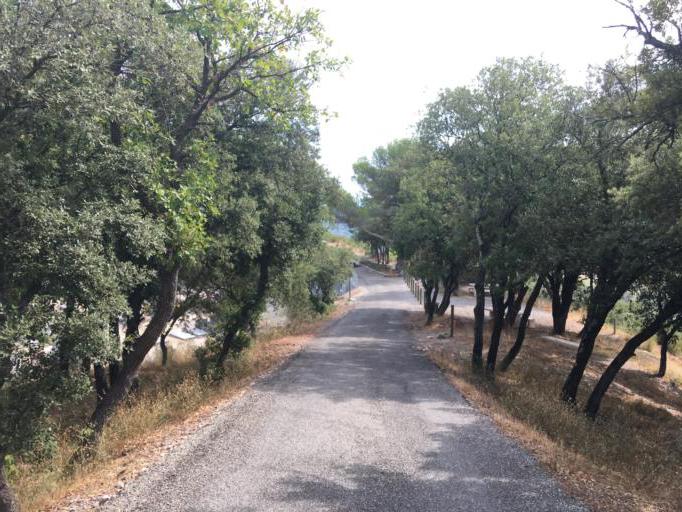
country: FR
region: Provence-Alpes-Cote d'Azur
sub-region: Departement du Var
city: Taradeau
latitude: 43.4534
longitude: 6.4334
